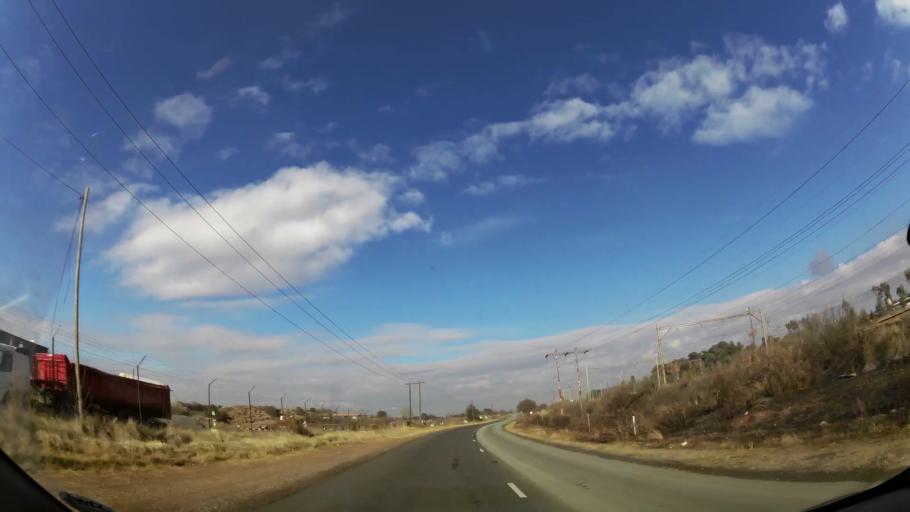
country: ZA
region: Gauteng
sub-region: Sedibeng District Municipality
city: Meyerton
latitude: -26.5104
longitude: 28.0543
